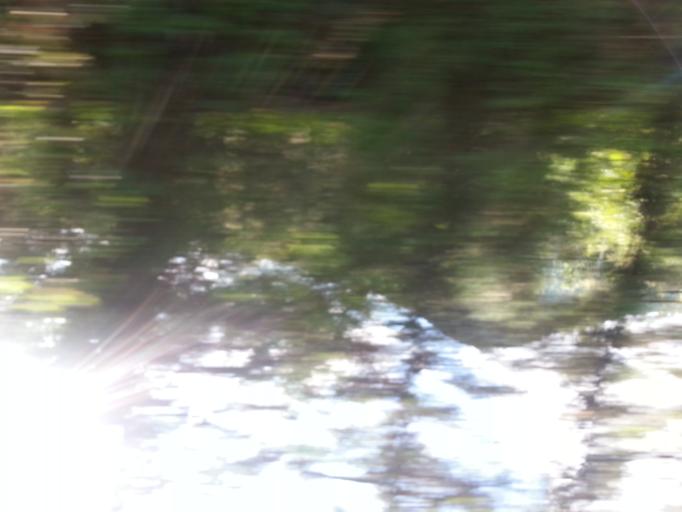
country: US
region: Tennessee
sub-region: Grainger County
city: Blaine
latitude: 36.1318
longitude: -83.7509
